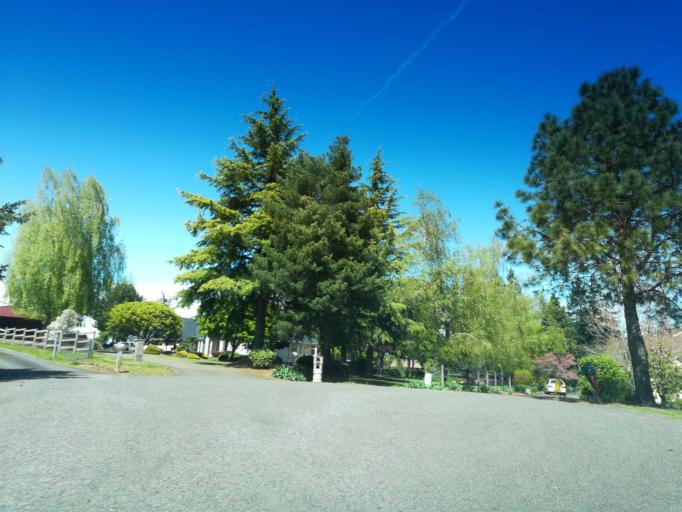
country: US
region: Oregon
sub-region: Clackamas County
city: Damascus
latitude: 45.4271
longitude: -122.4269
